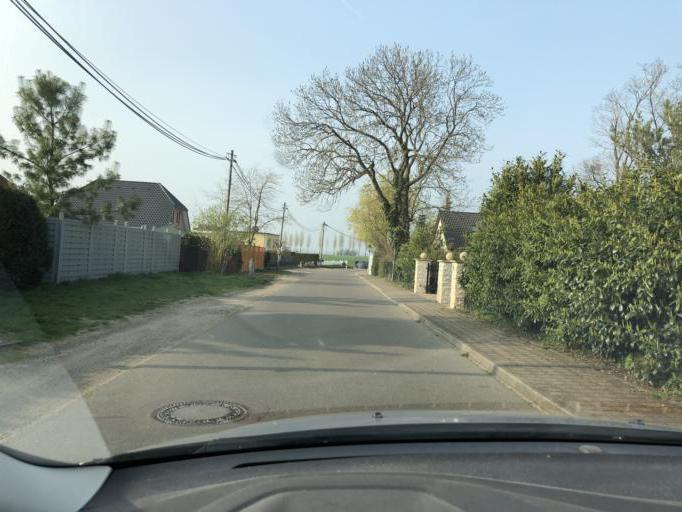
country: DE
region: Saxony-Anhalt
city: Zorbig
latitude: 51.6035
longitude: 12.1108
